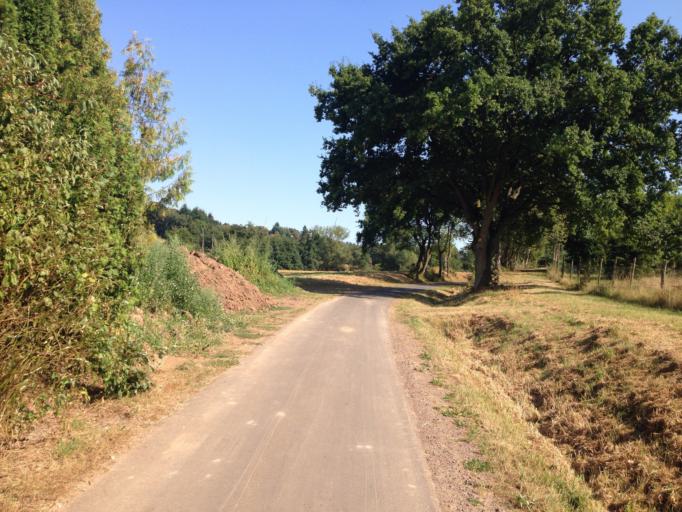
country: DE
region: Hesse
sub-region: Regierungsbezirk Giessen
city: Rabenau
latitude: 50.6662
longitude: 8.8785
